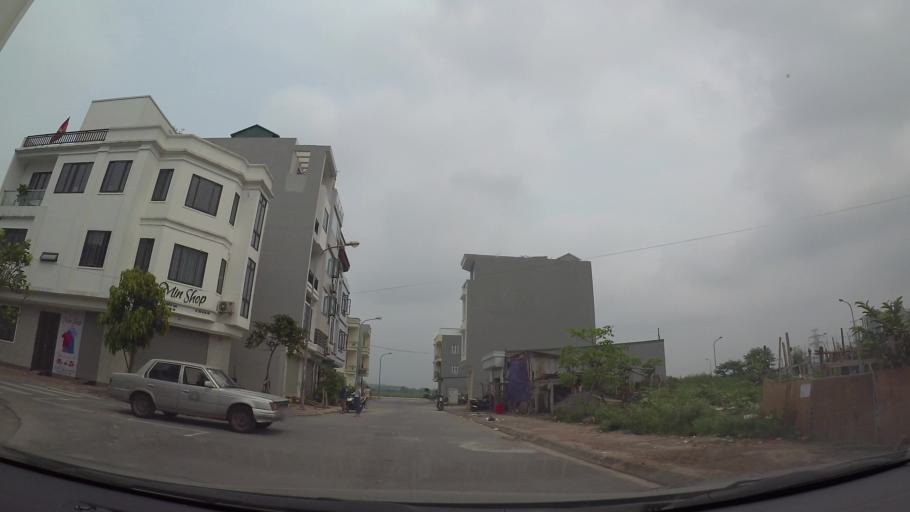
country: VN
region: Ha Noi
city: Trau Quy
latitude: 21.0646
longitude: 105.9140
